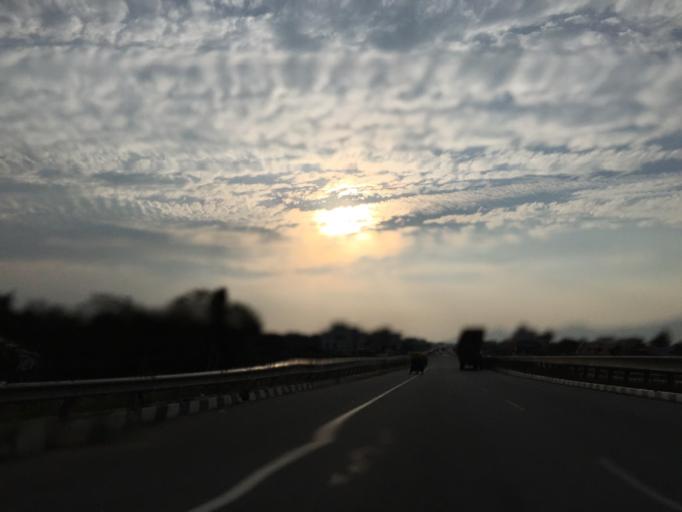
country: IN
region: Karnataka
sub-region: Kolar
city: Kolar
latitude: 13.1331
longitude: 78.1717
